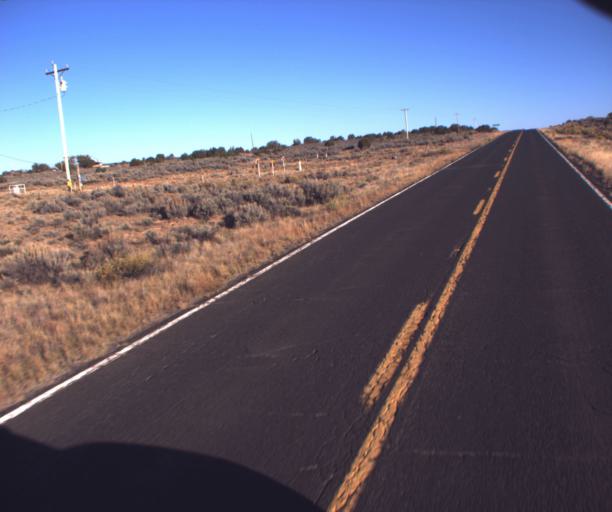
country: US
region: Arizona
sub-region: Apache County
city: Ganado
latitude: 35.5320
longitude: -109.5284
